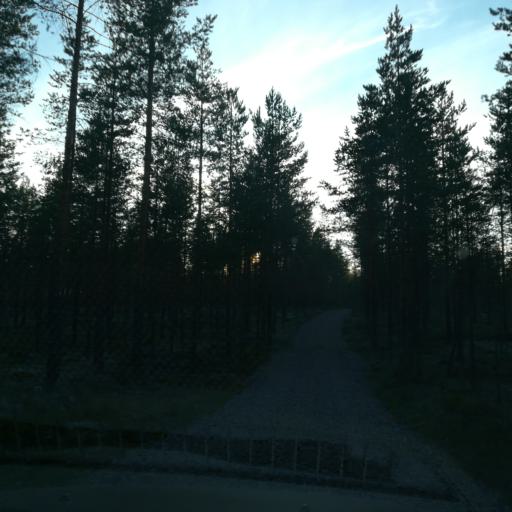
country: FI
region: Southern Savonia
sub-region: Mikkeli
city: Puumala
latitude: 61.4335
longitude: 28.4637
